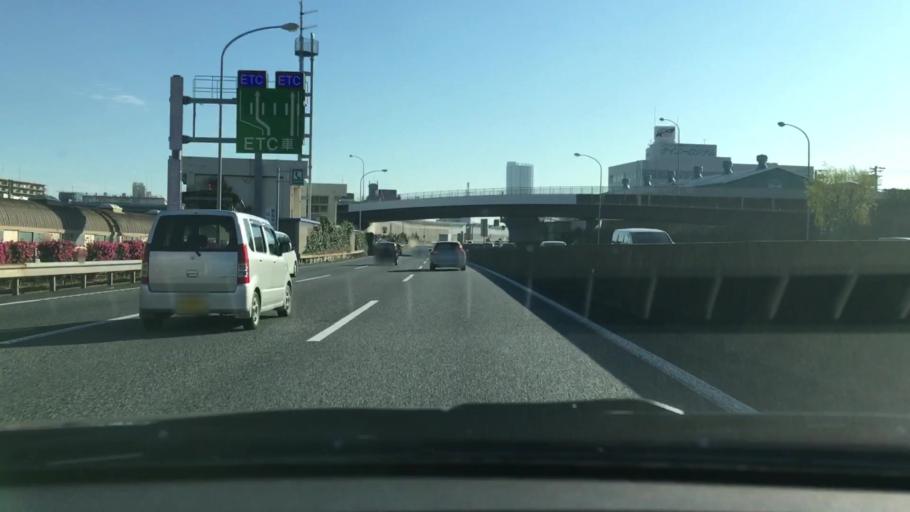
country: JP
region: Chiba
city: Funabashi
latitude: 35.6994
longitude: 139.9667
